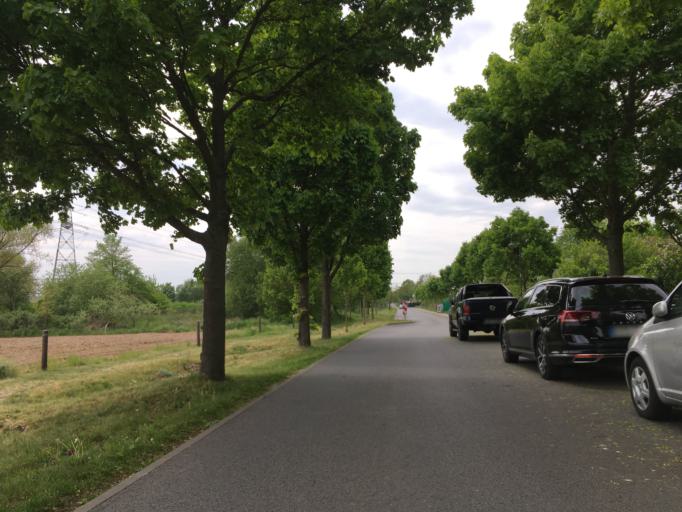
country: DE
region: Berlin
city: Buch
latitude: 52.6229
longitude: 13.5171
